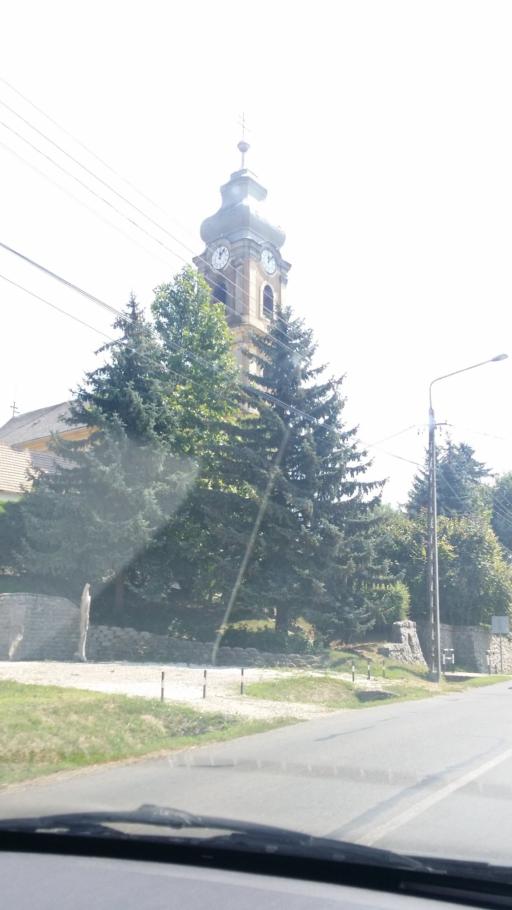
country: HU
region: Tolna
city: Iregszemcse
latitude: 46.6925
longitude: 18.1842
